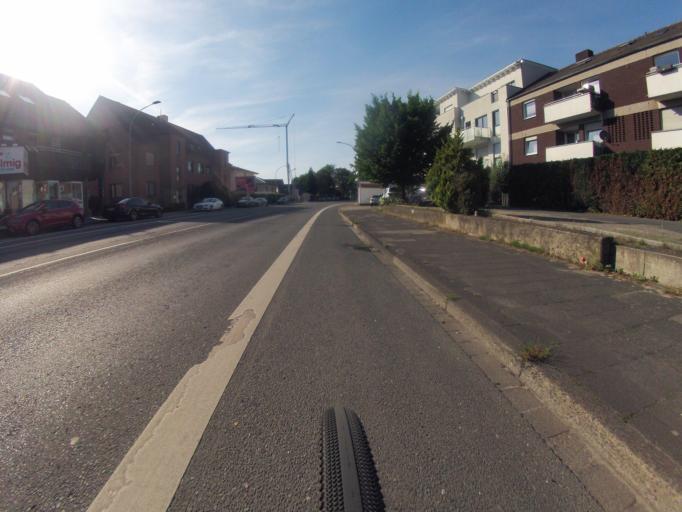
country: DE
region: North Rhine-Westphalia
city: Ibbenburen
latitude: 52.2708
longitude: 7.7102
